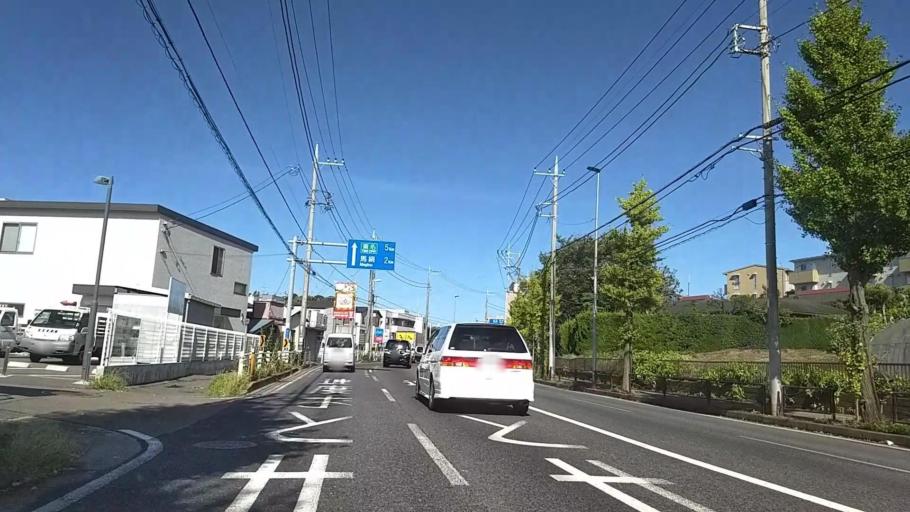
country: JP
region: Tokyo
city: Chofugaoka
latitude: 35.5734
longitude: 139.6134
